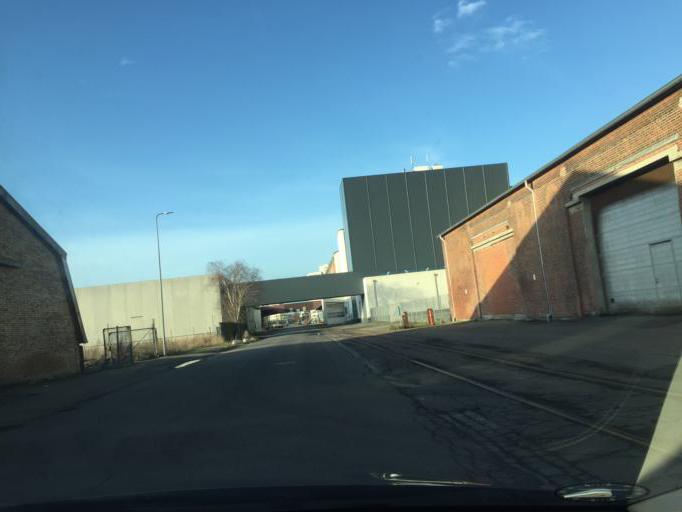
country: DK
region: South Denmark
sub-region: Vejle Kommune
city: Vejle
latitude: 55.7042
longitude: 9.5501
